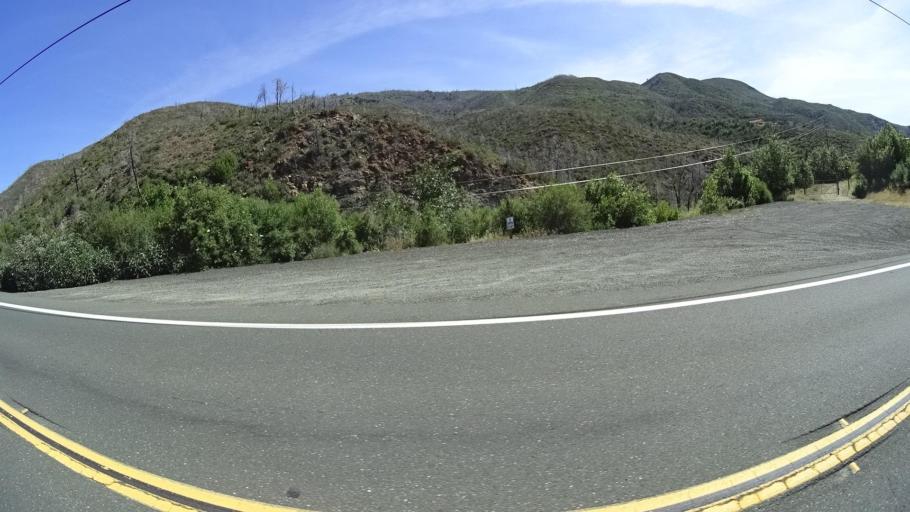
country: US
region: California
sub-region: Lake County
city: Cobb
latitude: 38.7916
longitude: -122.6967
